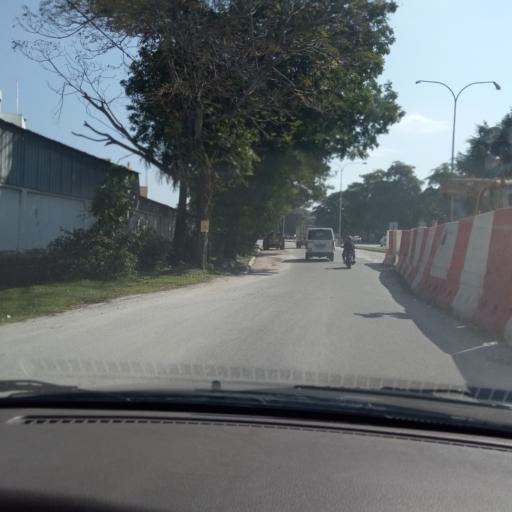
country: MY
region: Selangor
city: Kampong Baharu Balakong
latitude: 3.0195
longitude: 101.7652
